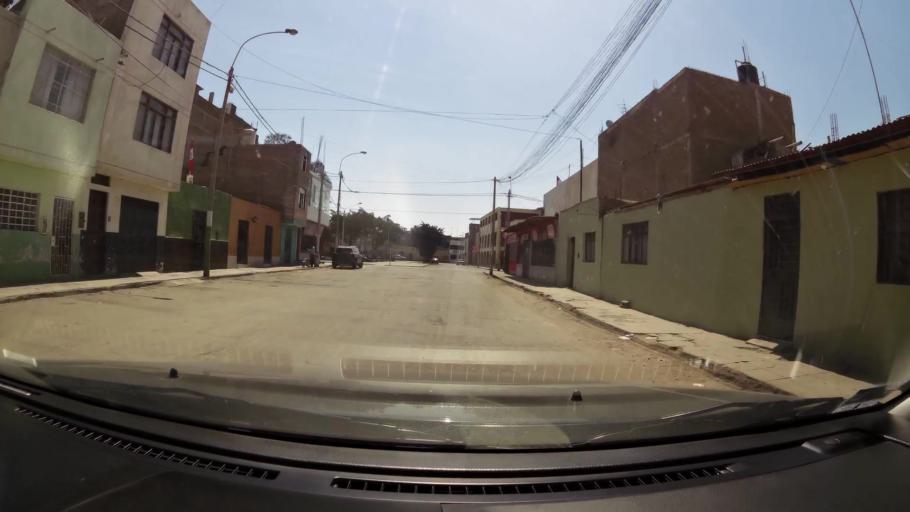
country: PE
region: Ica
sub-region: Provincia de Ica
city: Ica
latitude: -14.0693
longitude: -75.7263
